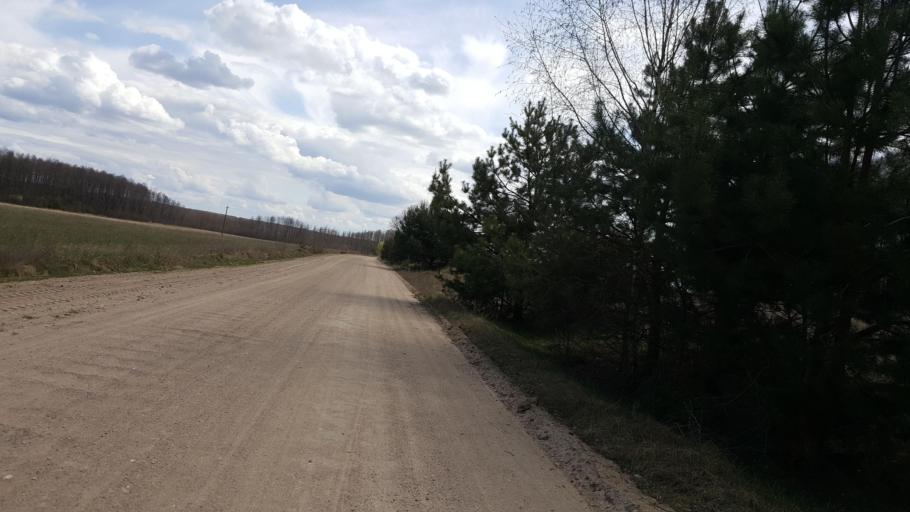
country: BY
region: Brest
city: Kamyanyets
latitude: 52.3642
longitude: 23.7262
